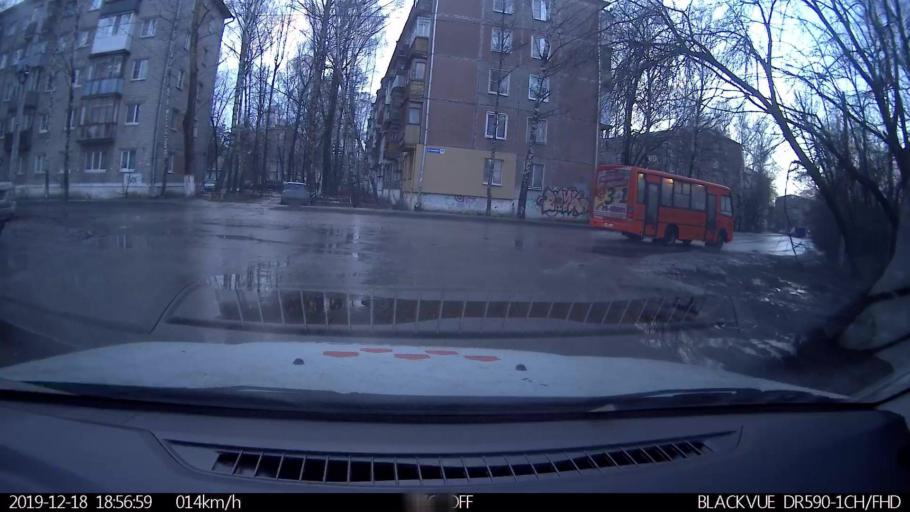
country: RU
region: Nizjnij Novgorod
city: Gorbatovka
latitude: 56.3390
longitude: 43.8430
